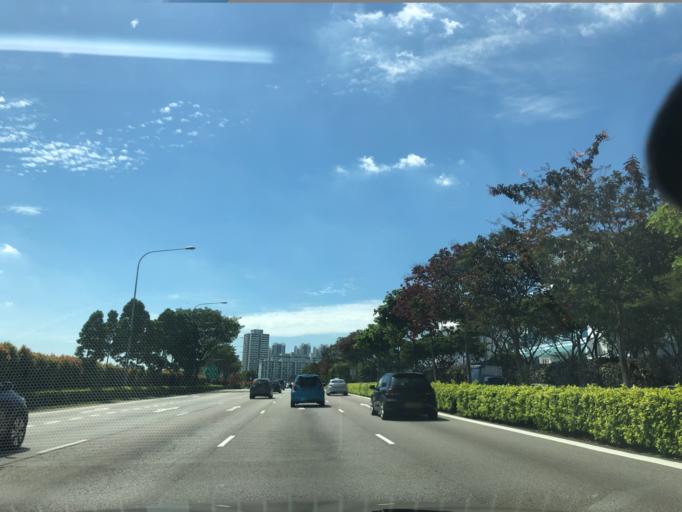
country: SG
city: Singapore
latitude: 1.3808
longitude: 103.8586
